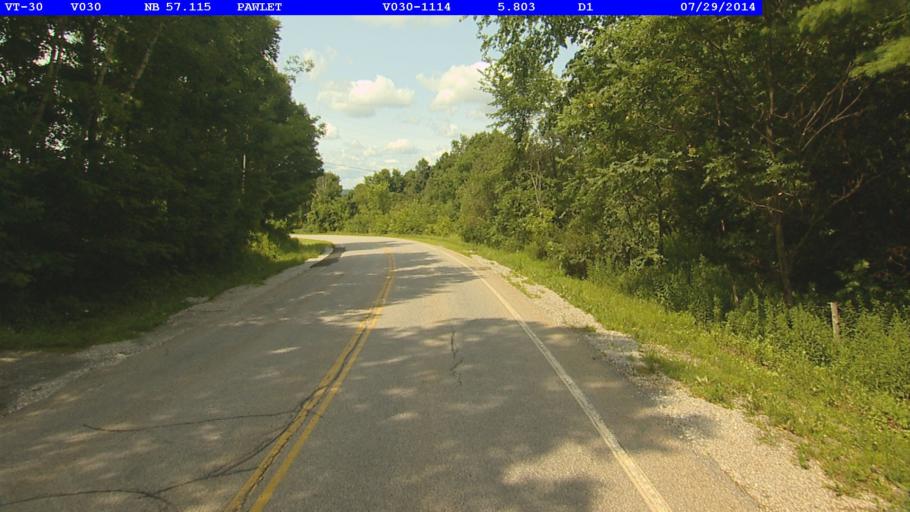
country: US
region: New York
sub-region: Washington County
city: Granville
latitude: 43.3810
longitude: -73.2034
